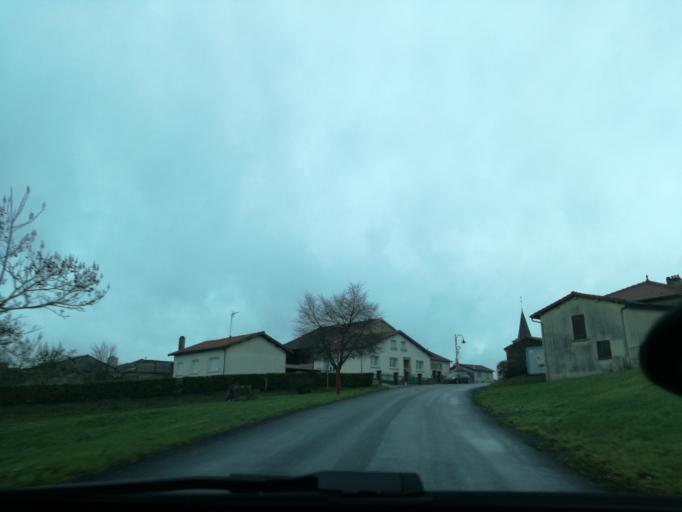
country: FR
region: Lorraine
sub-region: Departement de la Meuse
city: Revigny-sur-Ornain
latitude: 48.8335
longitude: 5.0439
